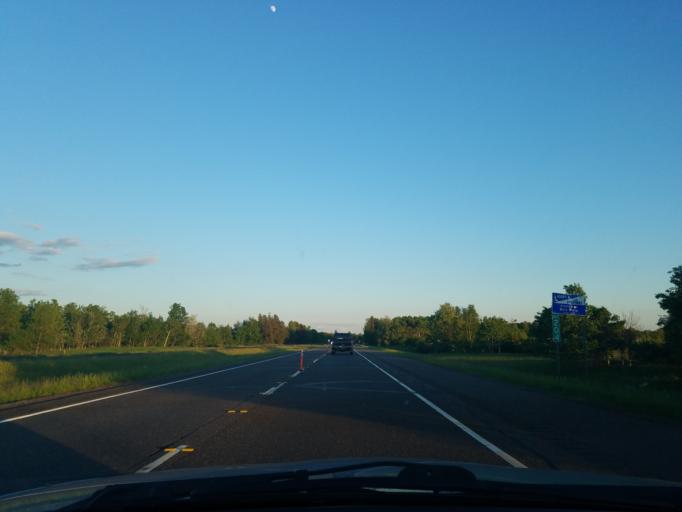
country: US
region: Minnesota
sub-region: Carlton County
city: Moose Lake
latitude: 46.2969
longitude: -92.8224
